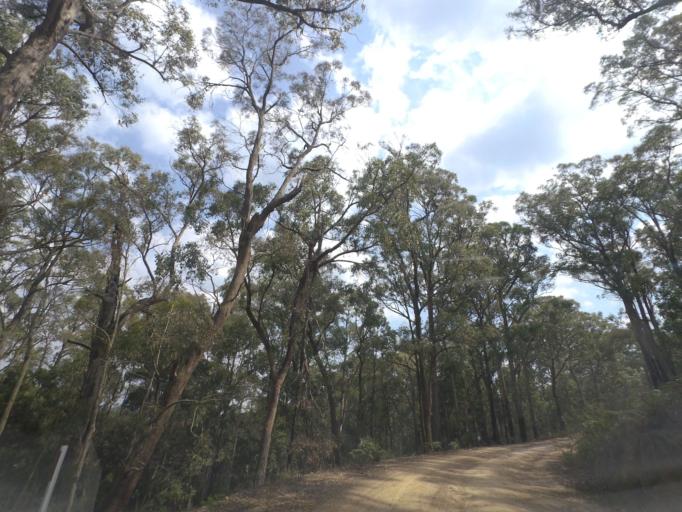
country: AU
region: Victoria
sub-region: Moorabool
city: Bacchus Marsh
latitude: -37.4649
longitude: 144.3759
